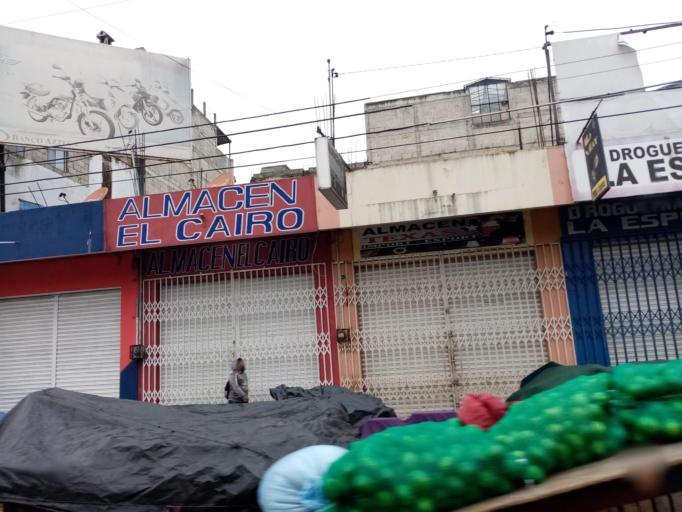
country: GT
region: Quetzaltenango
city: Quetzaltenango
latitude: 14.8408
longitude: -91.5209
